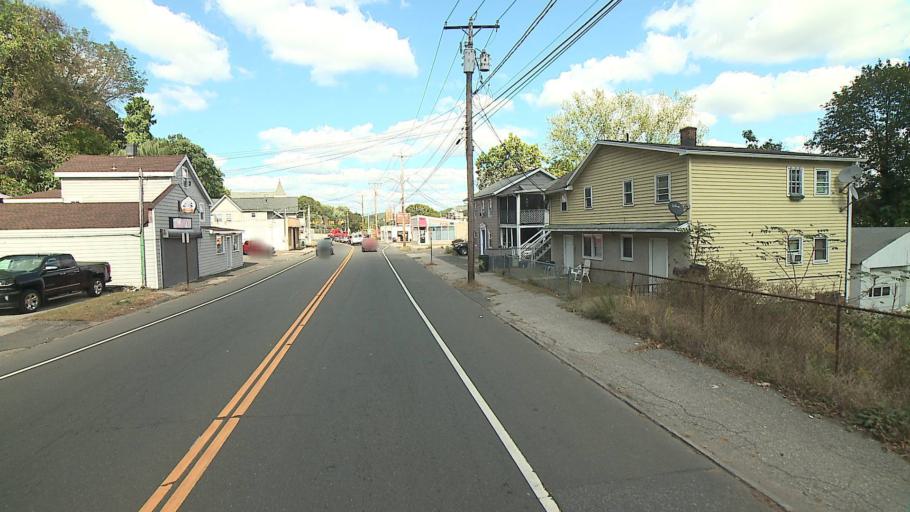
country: US
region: Connecticut
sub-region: New Haven County
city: Ansonia
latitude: 41.3397
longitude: -73.0823
